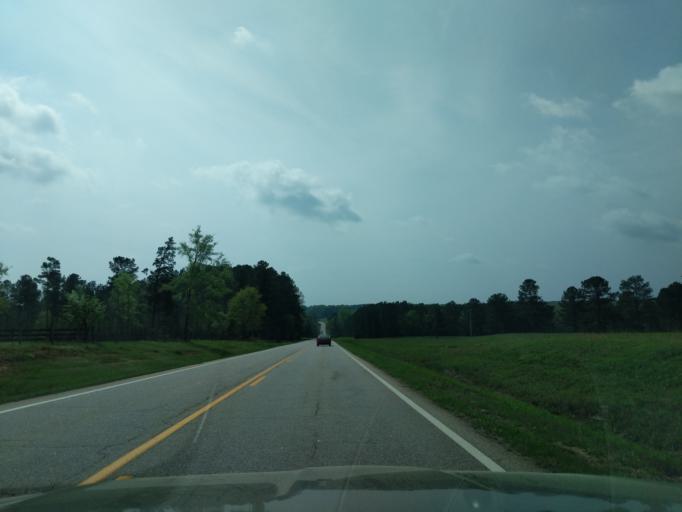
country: US
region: Georgia
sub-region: Lincoln County
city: Lincolnton
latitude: 33.8023
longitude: -82.3897
